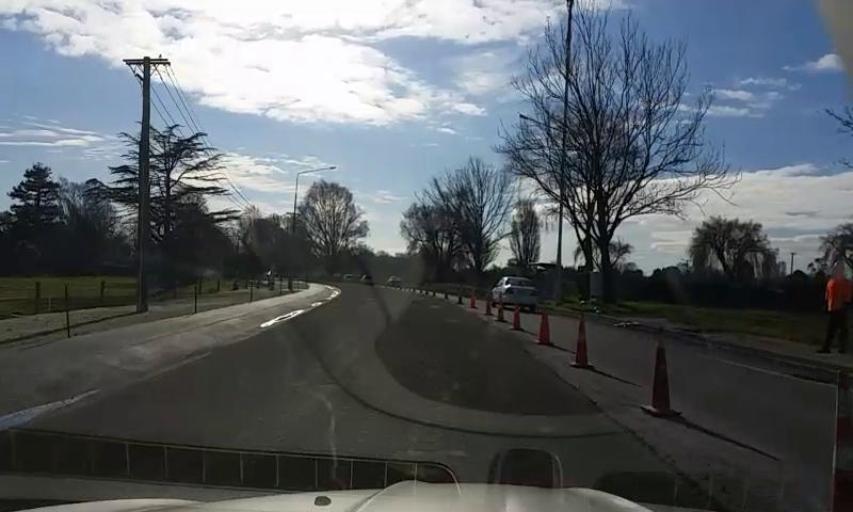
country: NZ
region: Canterbury
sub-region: Christchurch City
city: Christchurch
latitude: -43.5046
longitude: 172.6816
